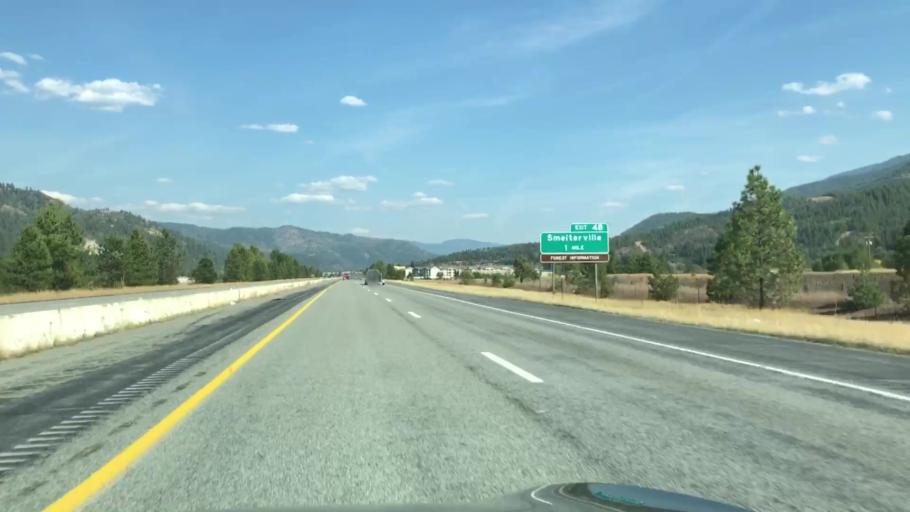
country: US
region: Idaho
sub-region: Shoshone County
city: Pinehurst
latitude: 47.5463
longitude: -116.2018
